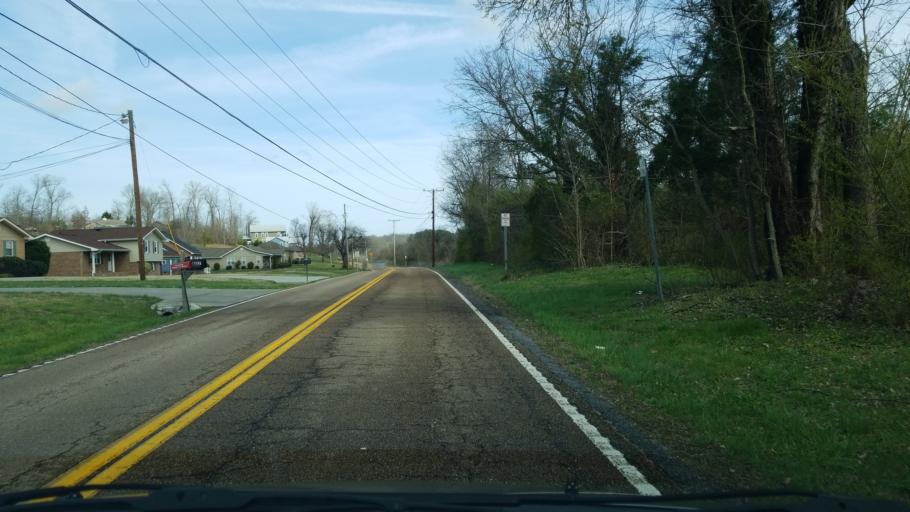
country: US
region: Tennessee
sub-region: Hamilton County
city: Harrison
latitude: 35.1526
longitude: -85.0616
